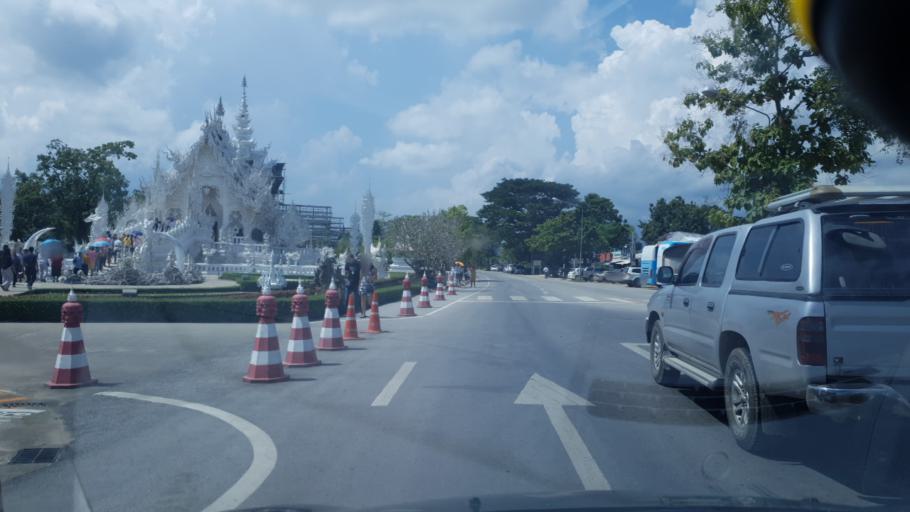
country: TH
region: Chiang Rai
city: Mae Lao
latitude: 19.8243
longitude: 99.7641
